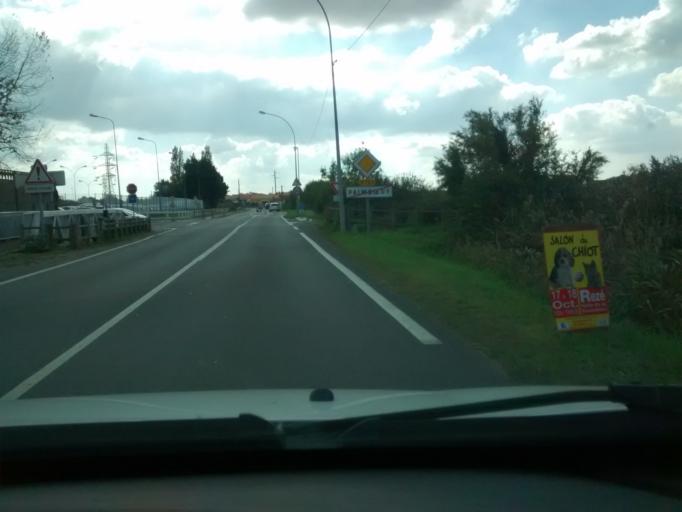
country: FR
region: Pays de la Loire
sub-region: Departement de la Loire-Atlantique
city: Saint-Paimboeuf
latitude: 47.2812
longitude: -2.0155
